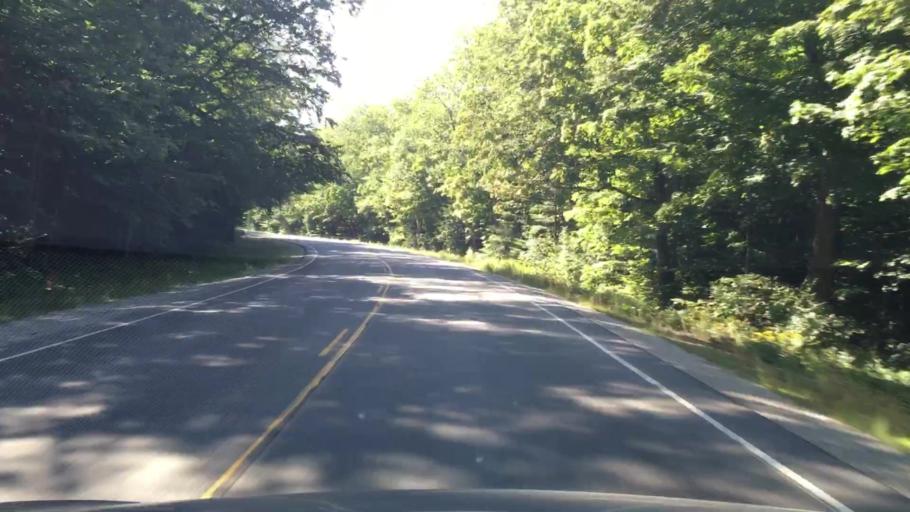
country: US
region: New Hampshire
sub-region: Carroll County
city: Tamworth
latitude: 43.9974
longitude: -71.3823
